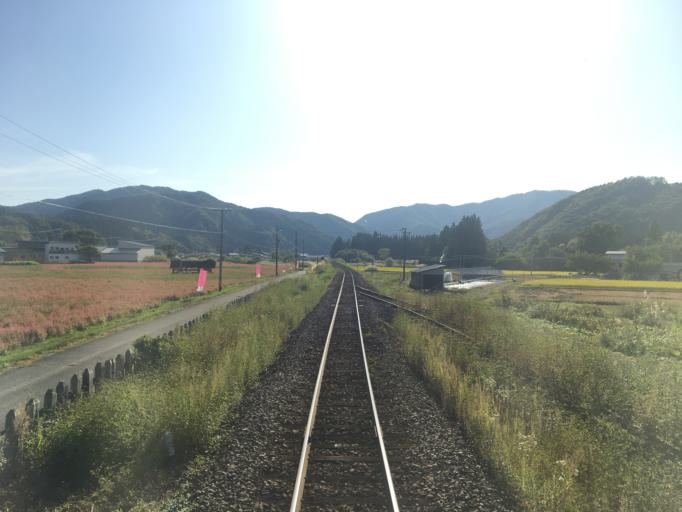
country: JP
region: Akita
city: Kakunodatemachi
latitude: 39.7437
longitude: 140.5899
